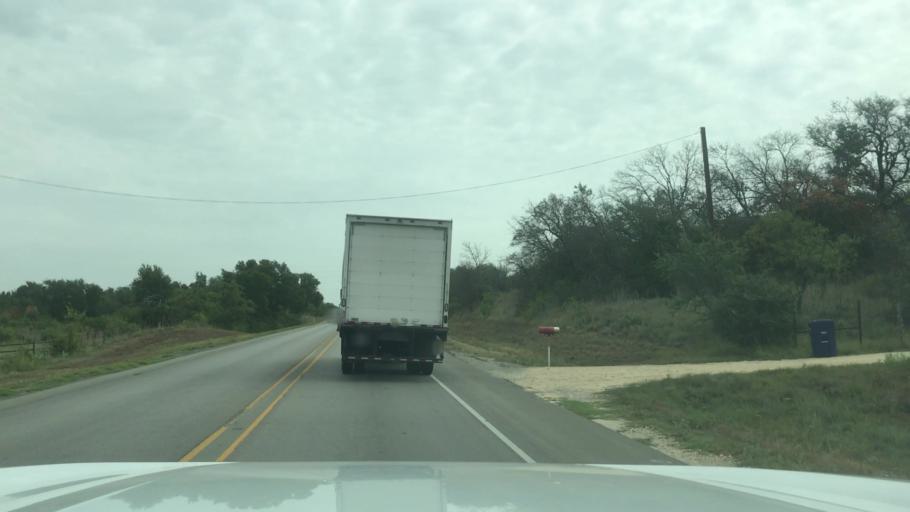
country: US
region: Texas
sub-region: Erath County
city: Dublin
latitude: 32.0883
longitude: -98.4279
